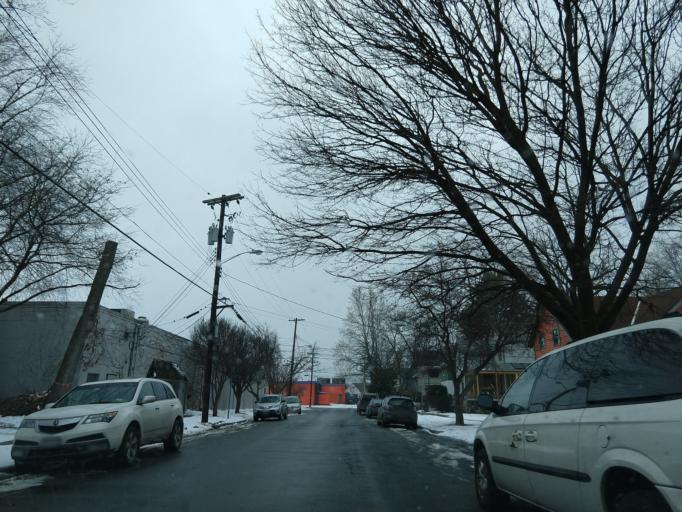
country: US
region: New York
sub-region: Tompkins County
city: Ithaca
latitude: 42.4470
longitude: -76.5042
